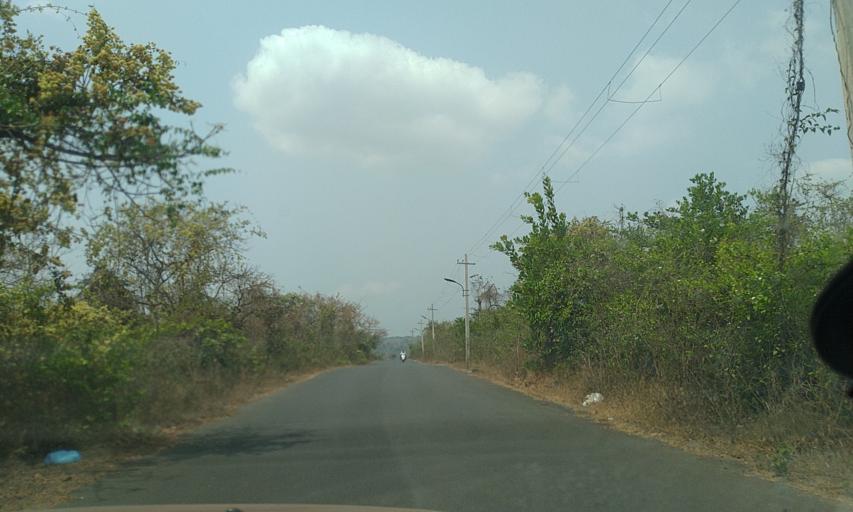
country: IN
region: Goa
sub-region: North Goa
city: Goa Velha
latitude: 15.4820
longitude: 73.8959
